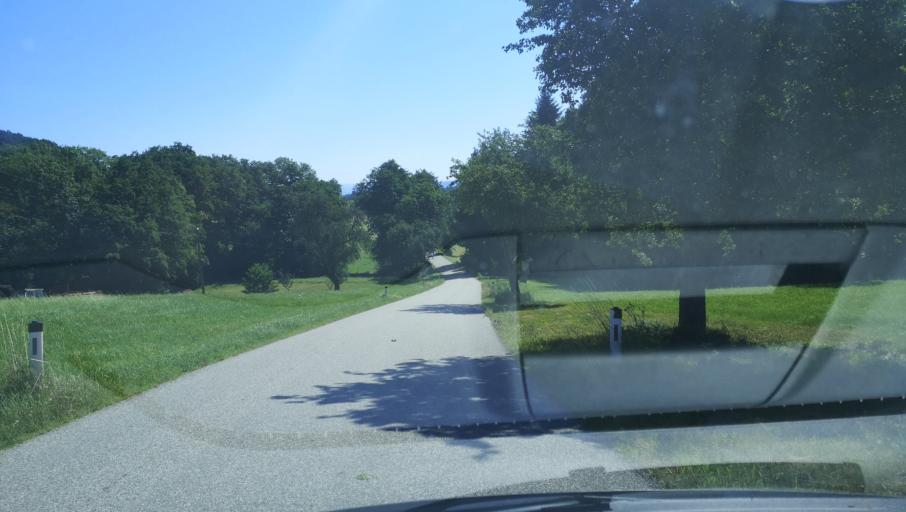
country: AT
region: Lower Austria
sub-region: Politischer Bezirk Melk
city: Blindenmarkt
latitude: 48.1600
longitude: 15.0102
